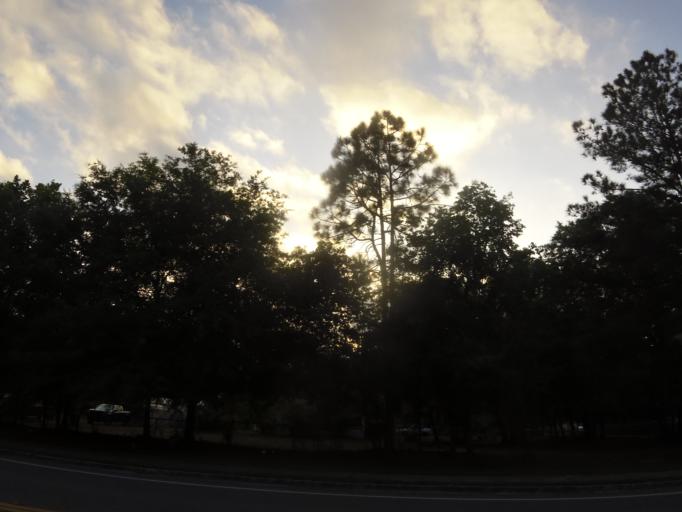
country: US
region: Florida
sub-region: Duval County
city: Jacksonville
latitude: 30.4512
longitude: -81.6131
